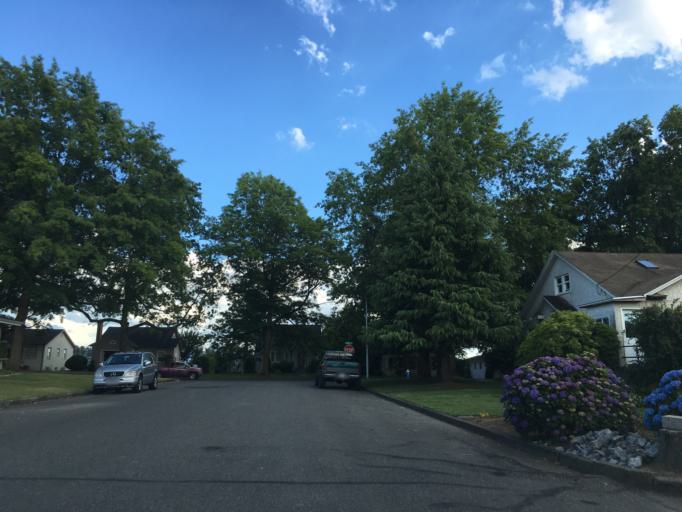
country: US
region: Washington
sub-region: Whatcom County
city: Lynden
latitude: 48.9406
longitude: -122.4622
